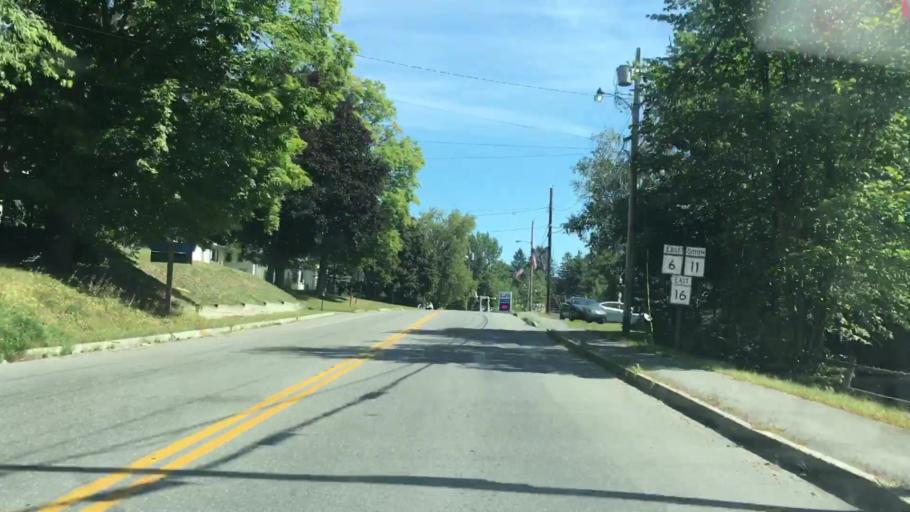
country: US
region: Maine
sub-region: Piscataquis County
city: Milo
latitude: 45.2520
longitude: -68.9860
